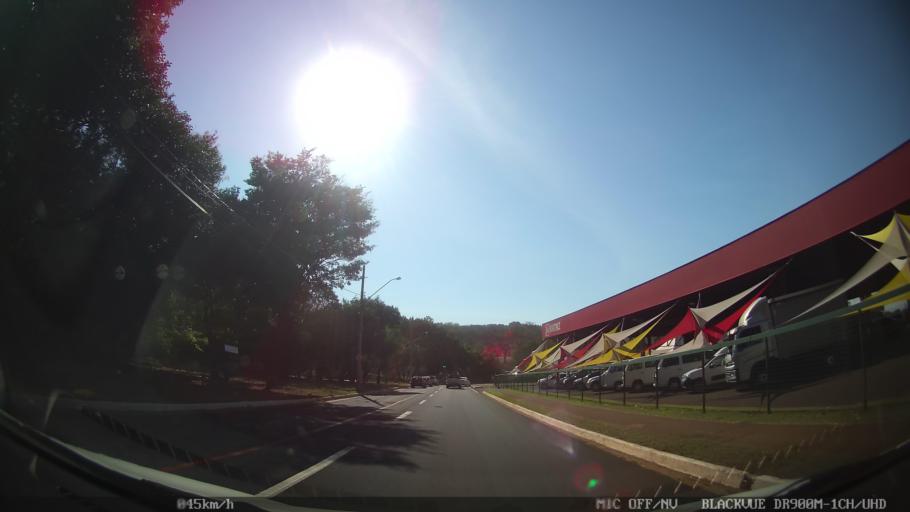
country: BR
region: Sao Paulo
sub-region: Ribeirao Preto
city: Ribeirao Preto
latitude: -21.2079
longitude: -47.7915
